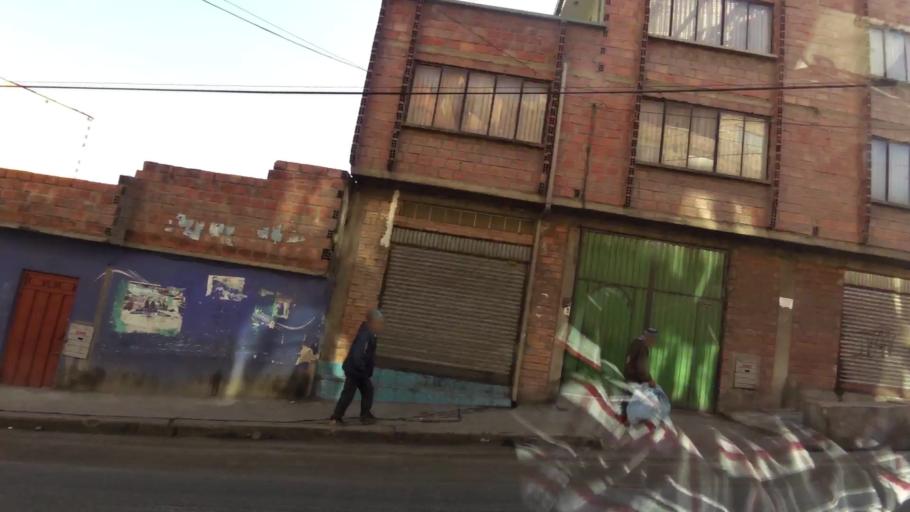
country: BO
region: La Paz
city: La Paz
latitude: -16.5023
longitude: -68.1521
